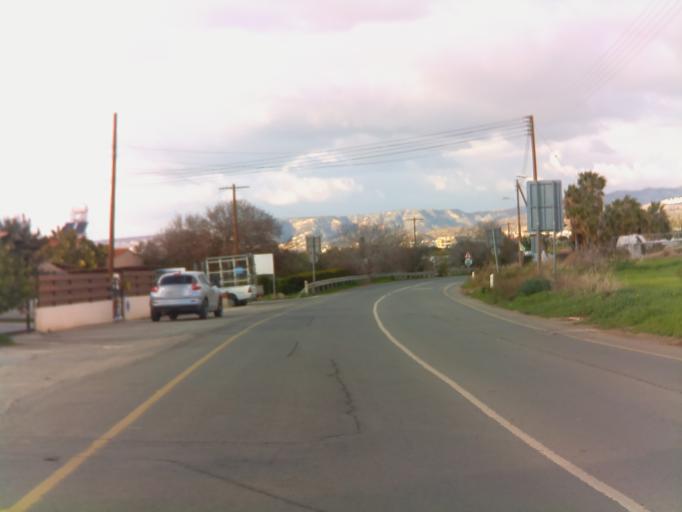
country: CY
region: Pafos
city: Chlorakas
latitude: 34.8107
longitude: 32.4104
